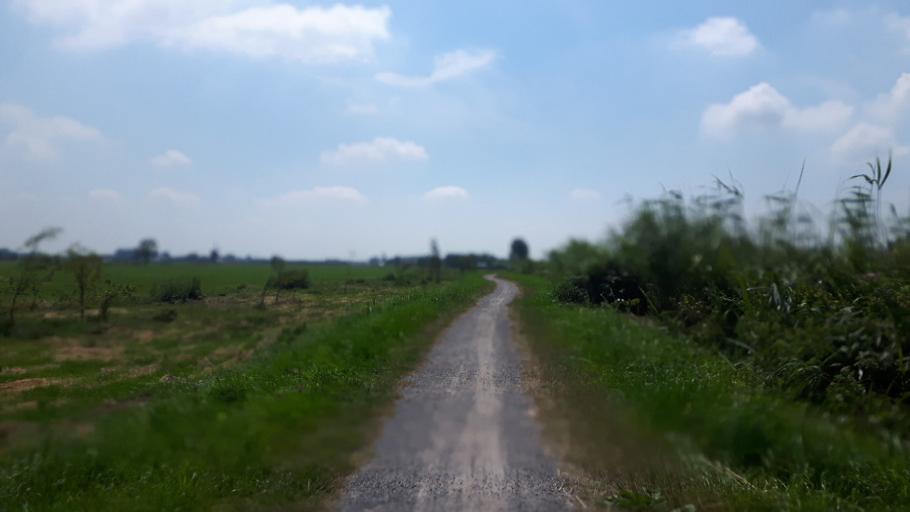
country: NL
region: Utrecht
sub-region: Gemeente Lopik
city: Lopik
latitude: 51.9286
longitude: 5.0005
